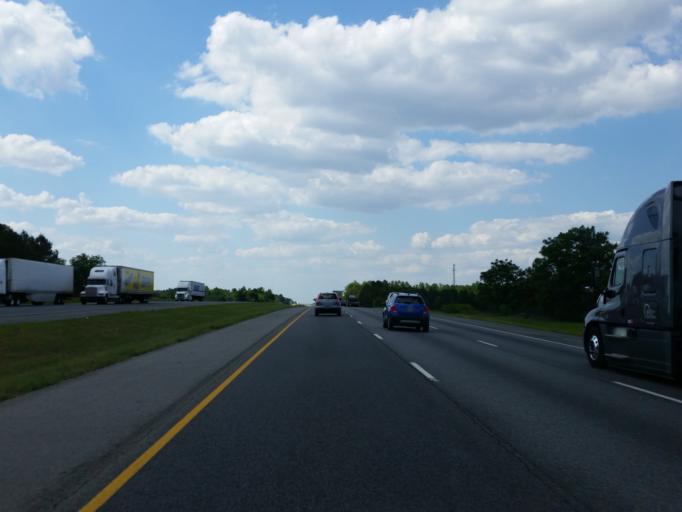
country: US
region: Georgia
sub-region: Crisp County
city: Cordele
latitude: 31.8799
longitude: -83.7274
